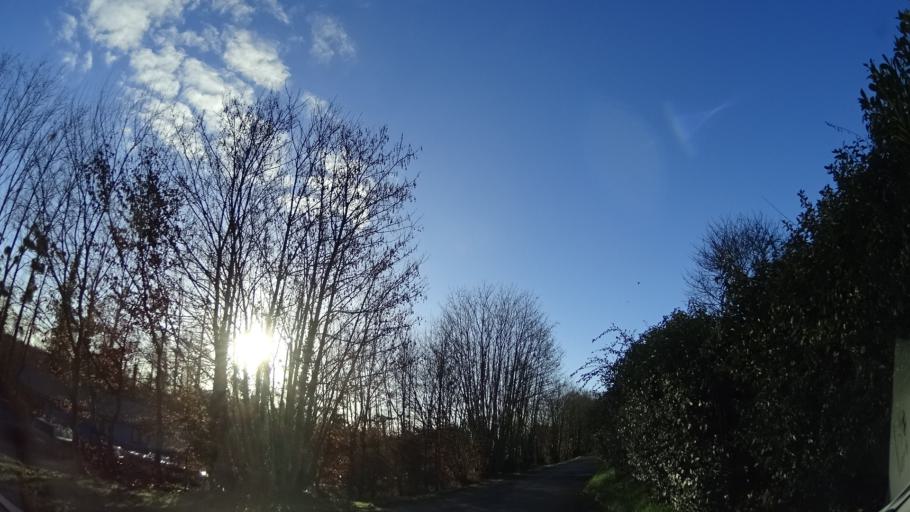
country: FR
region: Brittany
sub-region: Departement d'Ille-et-Vilaine
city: Betton
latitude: 48.1809
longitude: -1.6441
